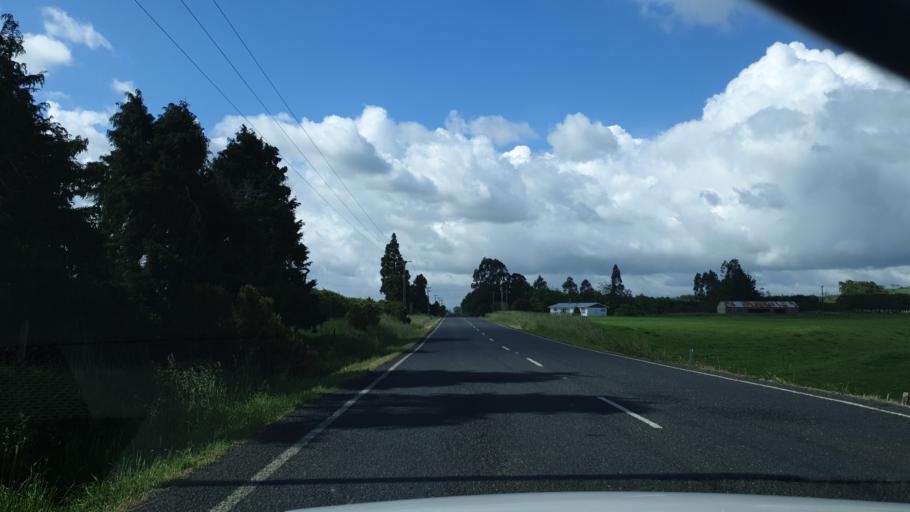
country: NZ
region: Waikato
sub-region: Hauraki District
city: Paeroa
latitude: -37.5081
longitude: 175.4955
